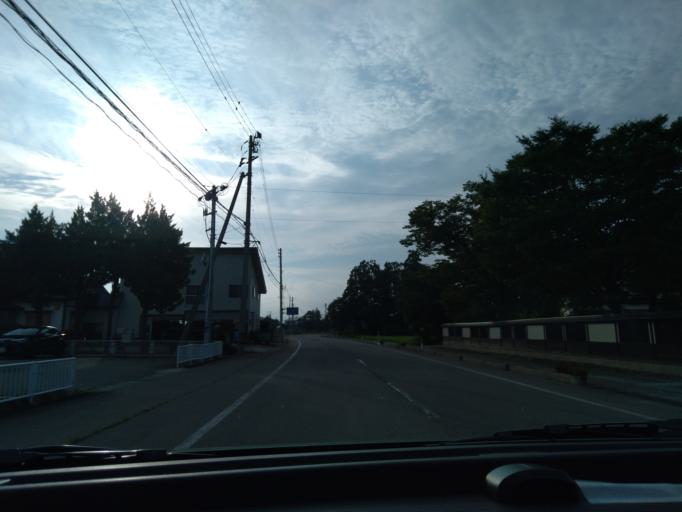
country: JP
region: Akita
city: Yokotemachi
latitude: 39.3872
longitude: 140.5279
